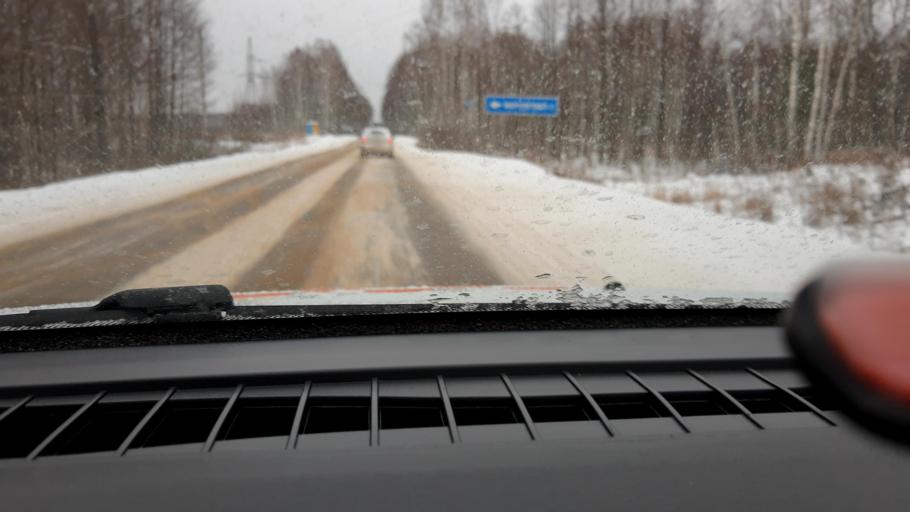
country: RU
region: Nizjnij Novgorod
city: Kstovo
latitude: 56.2834
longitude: 44.3107
